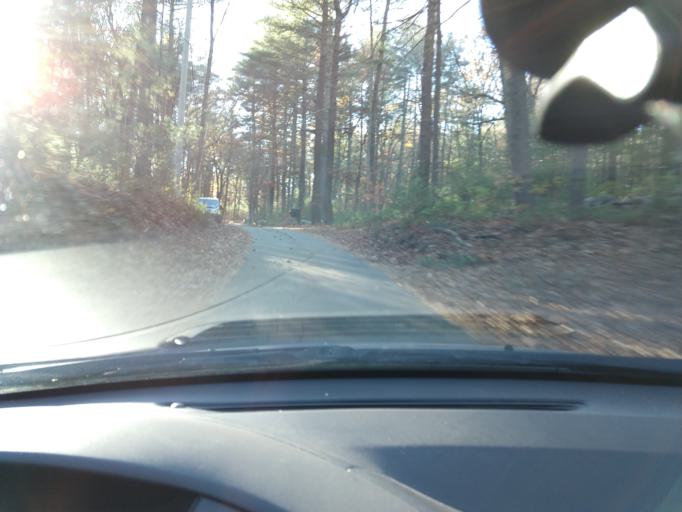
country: US
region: Massachusetts
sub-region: Middlesex County
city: Concord
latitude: 42.4893
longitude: -71.3273
